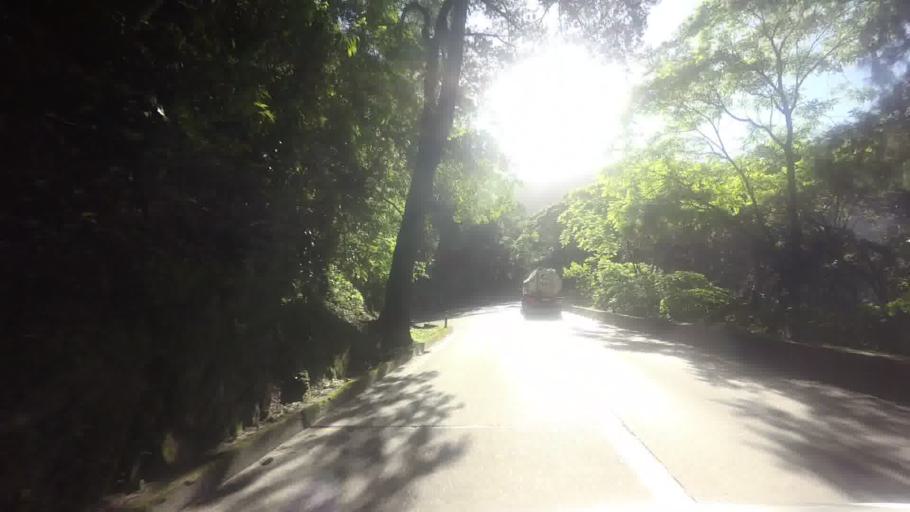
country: BR
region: Rio de Janeiro
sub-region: Petropolis
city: Petropolis
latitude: -22.5548
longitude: -43.2331
